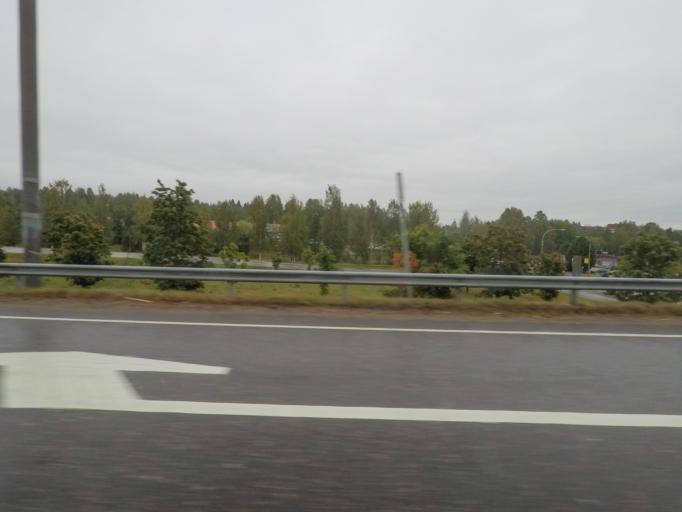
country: FI
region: Northern Savo
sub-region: Varkaus
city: Leppaevirta
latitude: 62.4896
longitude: 27.7672
